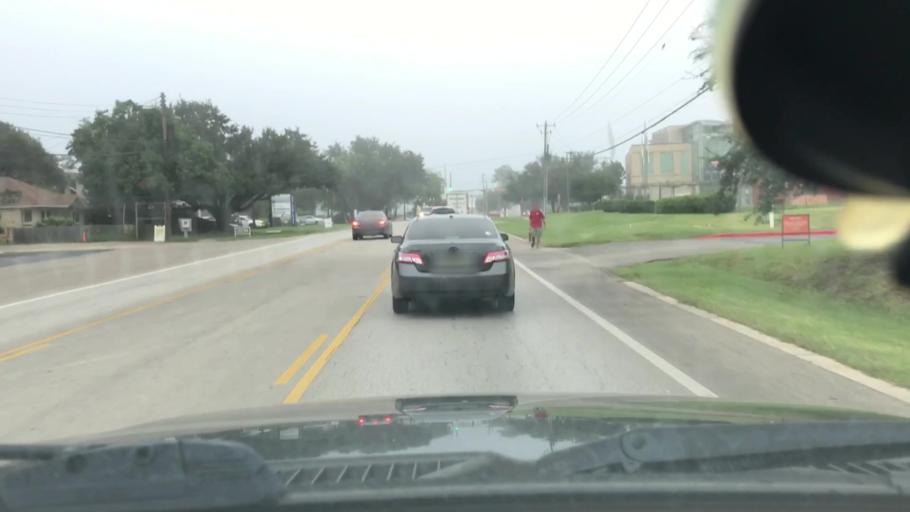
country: US
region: Texas
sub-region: Williamson County
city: Jollyville
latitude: 30.4426
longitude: -97.7748
